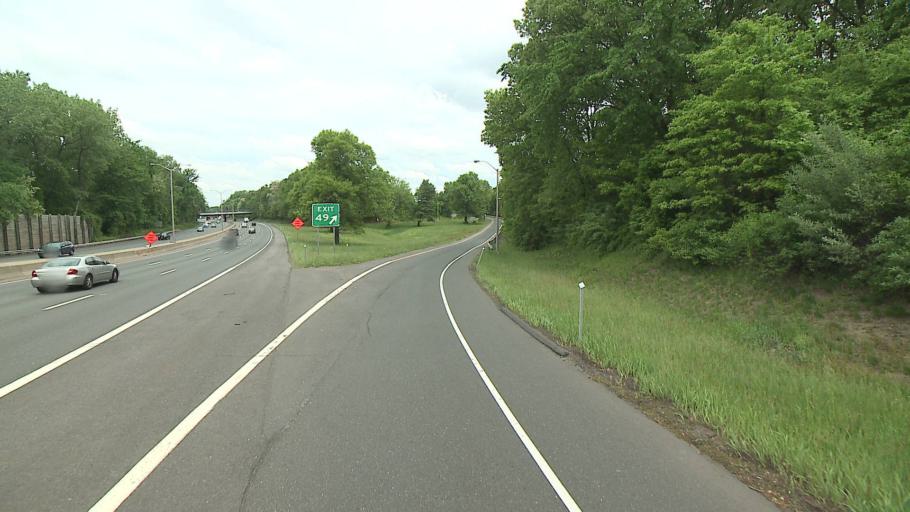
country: US
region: Connecticut
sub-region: Hartford County
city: Sherwood Manor
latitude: 42.0176
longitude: -72.5868
